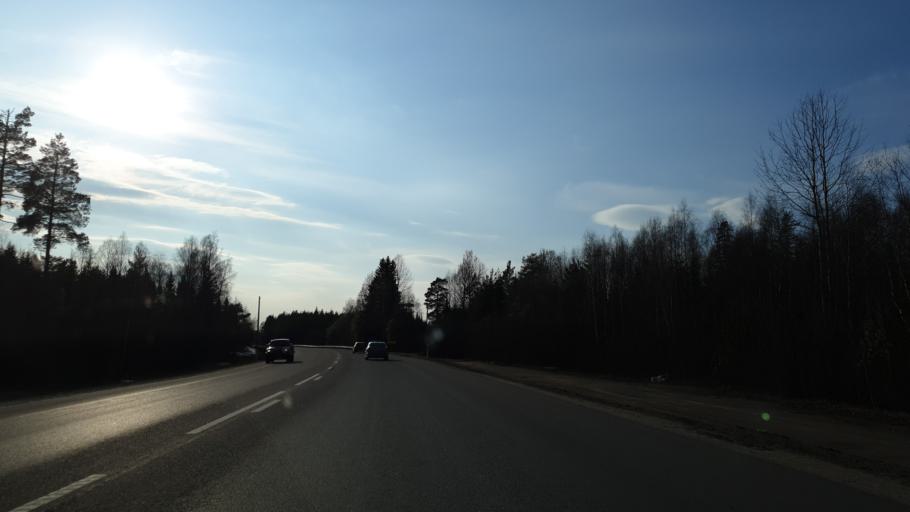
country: SE
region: Gaevleborg
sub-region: Hudiksvalls Kommun
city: Hudiksvall
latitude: 61.7148
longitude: 17.0613
